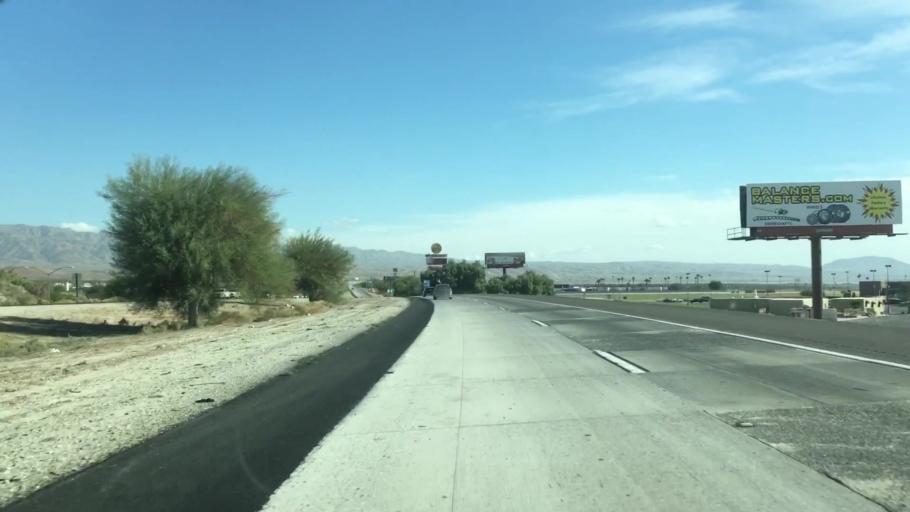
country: US
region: California
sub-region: Riverside County
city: Indio
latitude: 33.7151
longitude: -116.1862
